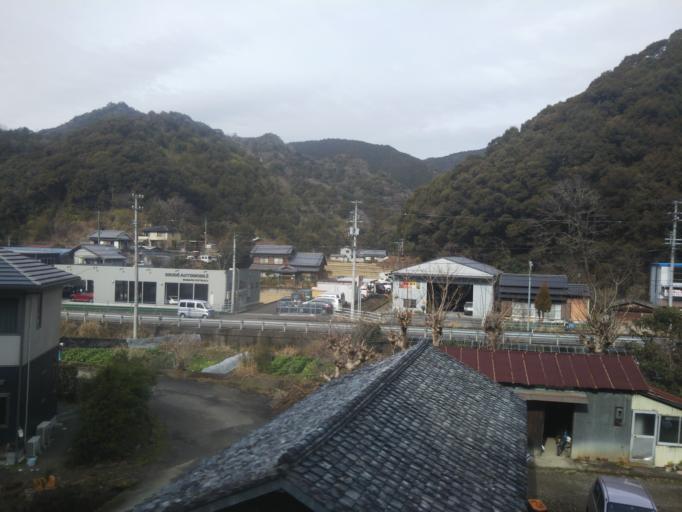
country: JP
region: Kochi
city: Nakamura
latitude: 32.9972
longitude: 132.9664
